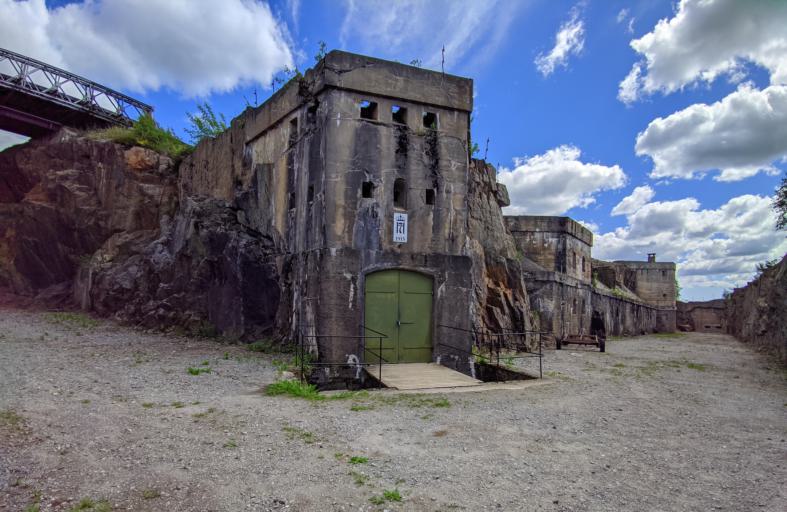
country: NO
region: Ostfold
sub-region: Eidsberg
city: Mysen
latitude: 59.5626
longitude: 11.3441
